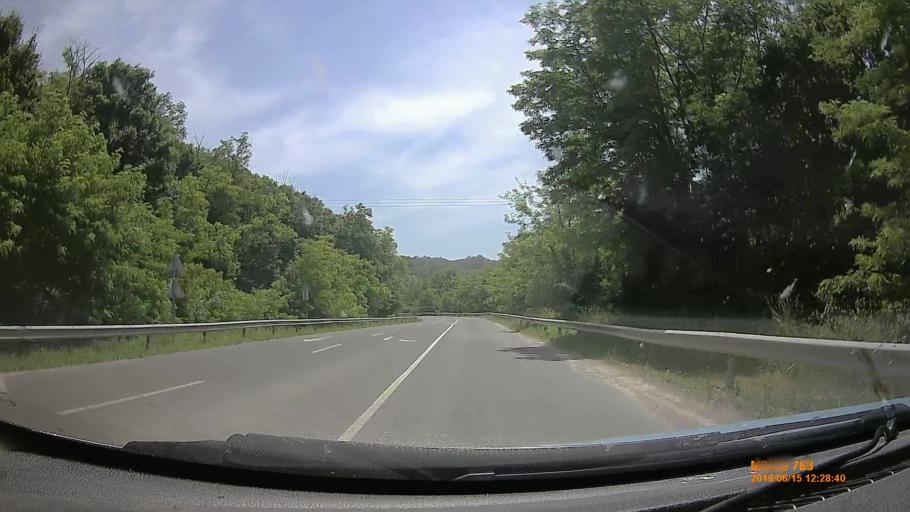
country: HU
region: Baranya
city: Buekkoesd
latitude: 46.1244
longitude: 18.0255
